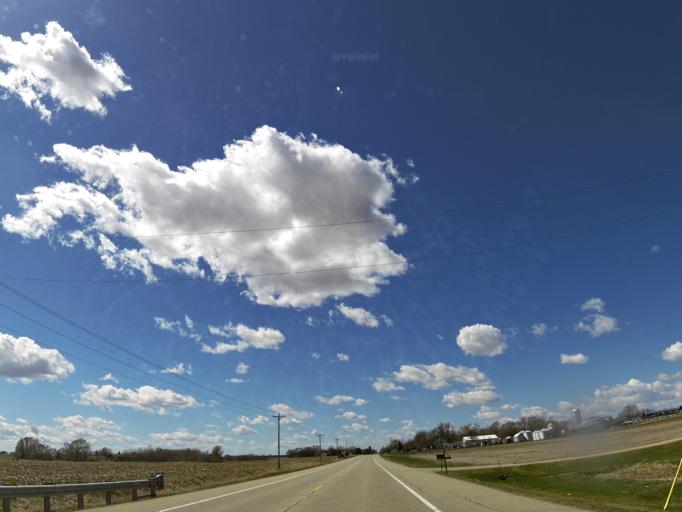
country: US
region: Minnesota
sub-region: Dakota County
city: Hastings
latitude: 44.7168
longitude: -92.9611
